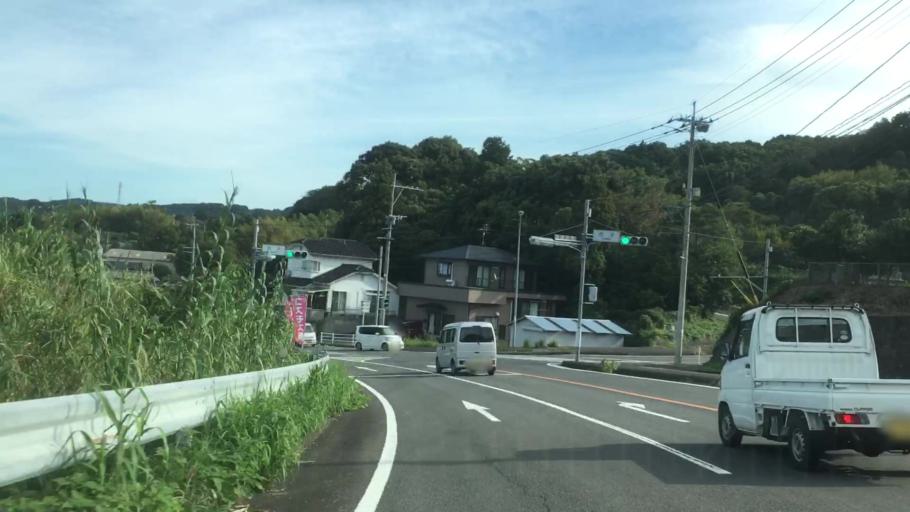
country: JP
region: Nagasaki
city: Sasebo
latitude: 33.0338
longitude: 129.6622
